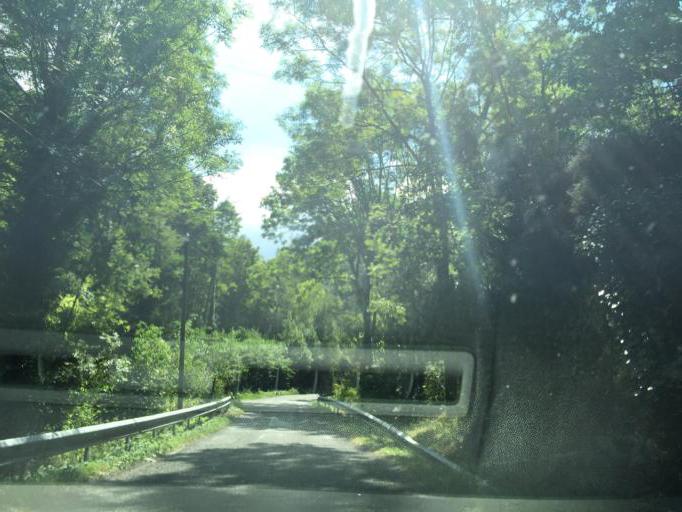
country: FR
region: Rhone-Alpes
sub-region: Departement de la Loire
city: Saint-Jean-Bonnefonds
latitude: 45.4224
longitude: 4.4395
